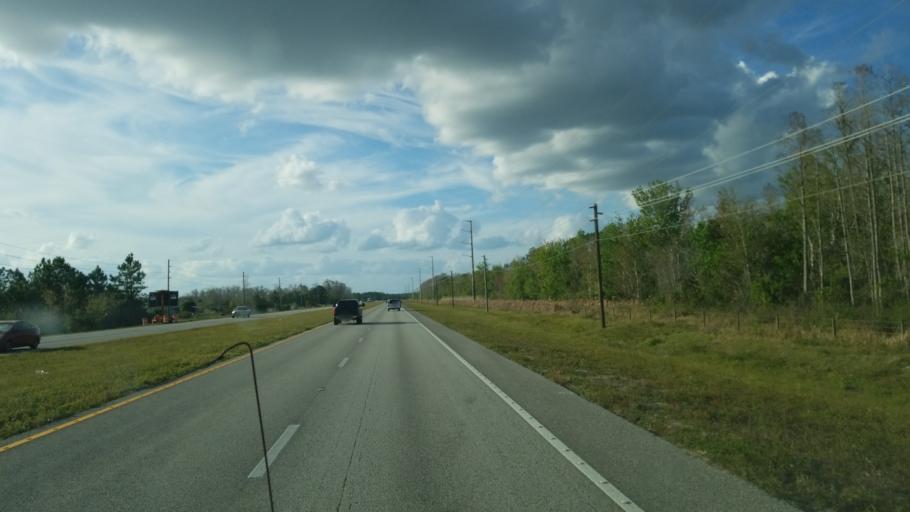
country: US
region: Florida
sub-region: Osceola County
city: Saint Cloud
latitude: 28.1606
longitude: -81.1160
